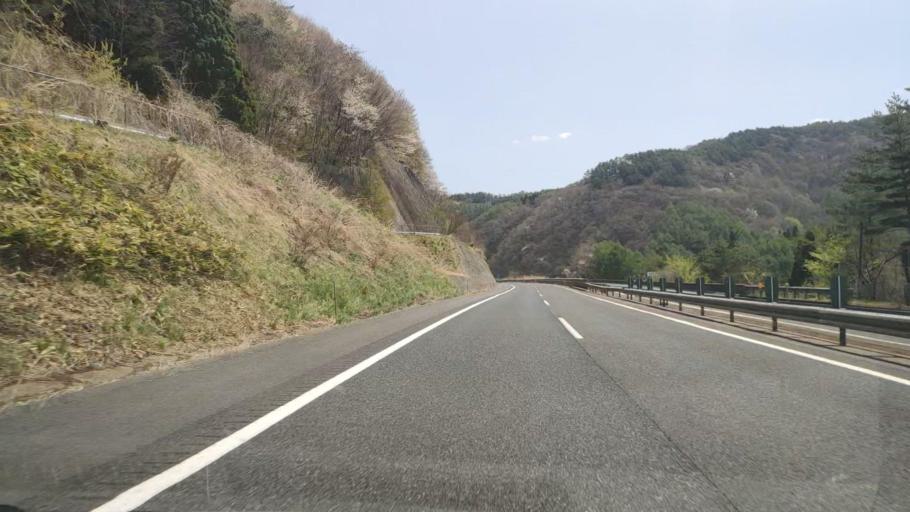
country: JP
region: Iwate
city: Ichinohe
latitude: 40.2229
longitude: 141.2553
